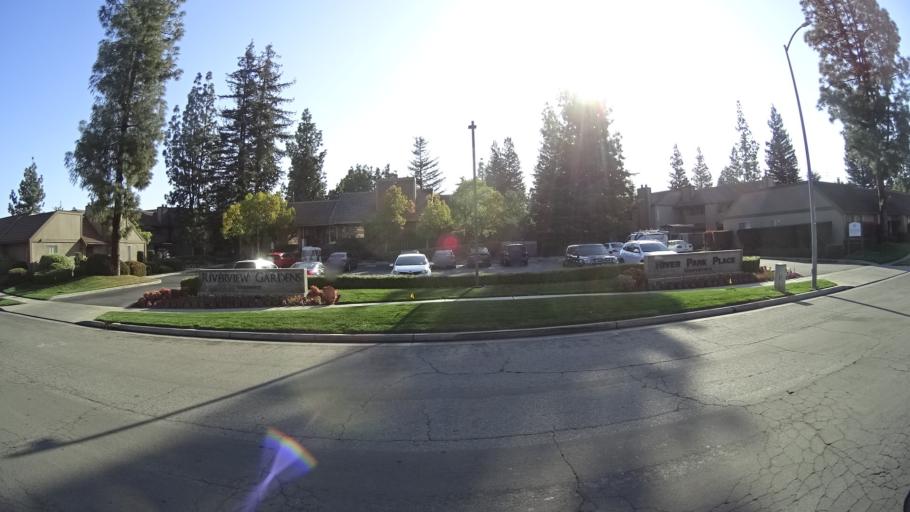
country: US
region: California
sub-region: Fresno County
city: Clovis
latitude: 36.8531
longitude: -119.7965
